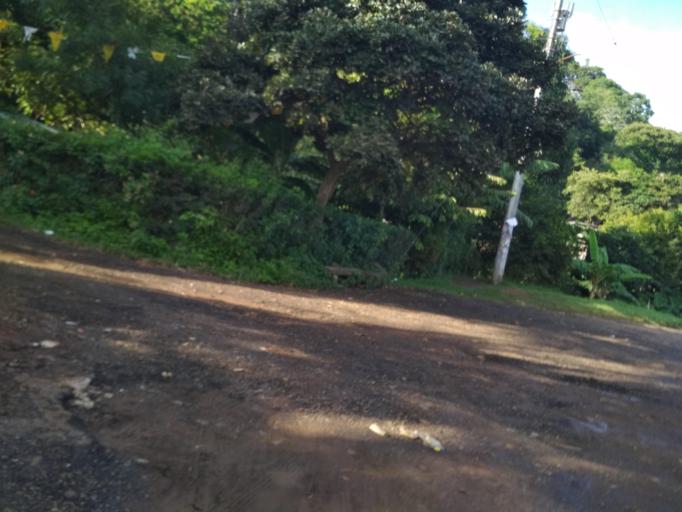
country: MX
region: Veracruz
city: Catemaco
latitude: 18.3905
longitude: -95.1239
